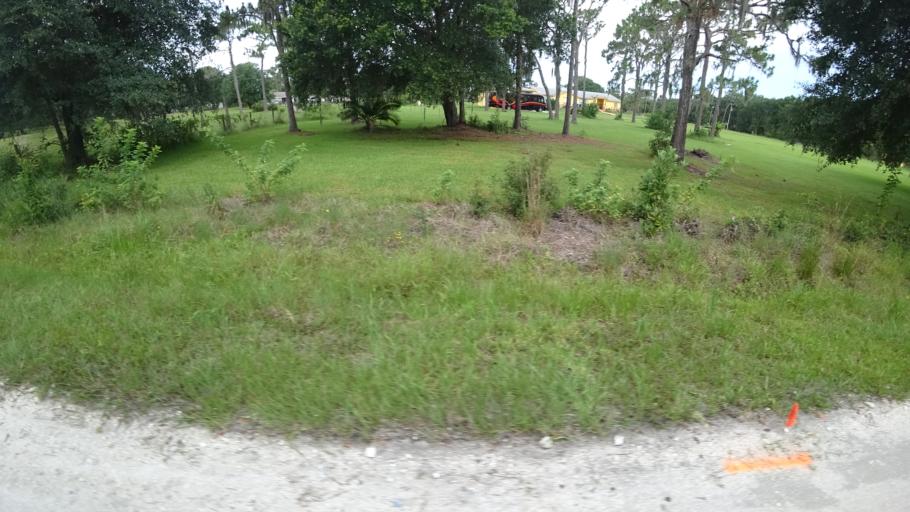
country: US
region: Florida
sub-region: Sarasota County
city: The Meadows
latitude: 27.4507
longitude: -82.2787
